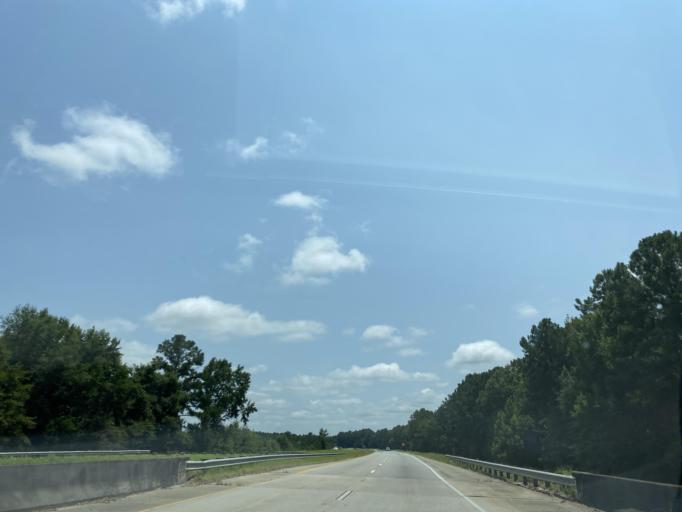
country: US
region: Georgia
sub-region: Telfair County
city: Lumber City
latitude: 31.9153
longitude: -82.6718
